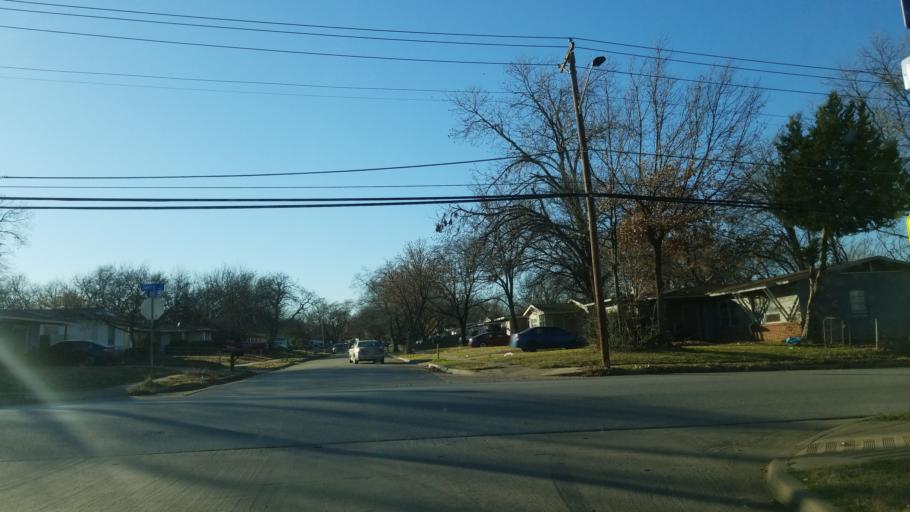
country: US
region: Texas
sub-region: Tarrant County
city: Arlington
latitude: 32.7297
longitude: -97.0714
